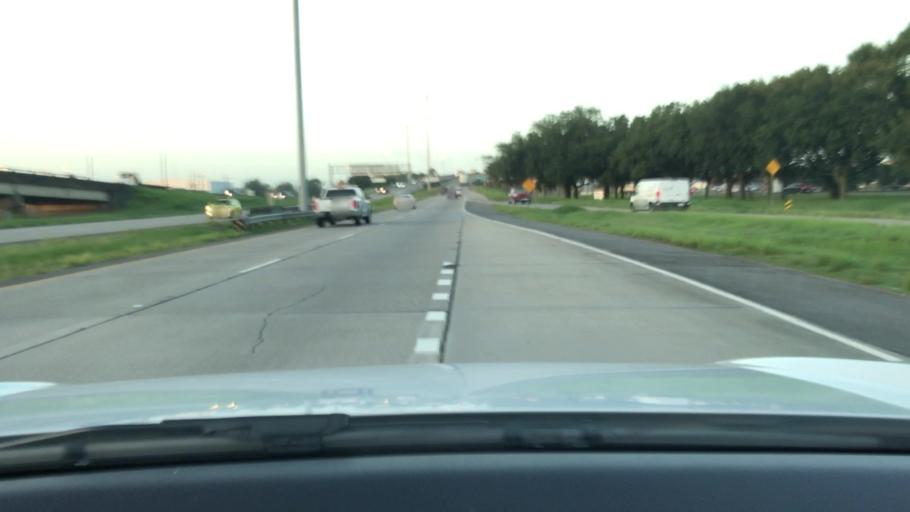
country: US
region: Louisiana
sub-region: West Baton Rouge Parish
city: Port Allen
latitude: 30.4379
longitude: -91.2089
